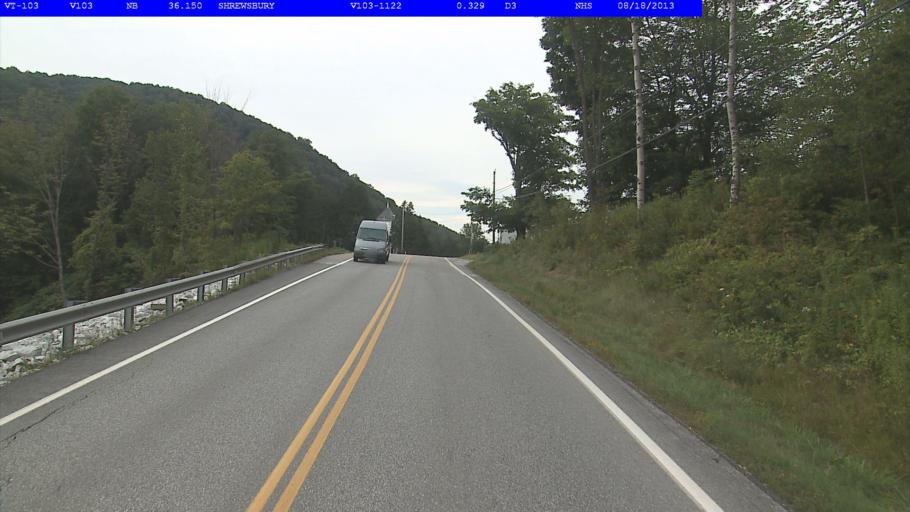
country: US
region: Vermont
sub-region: Rutland County
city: Rutland
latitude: 43.4786
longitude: -72.8929
